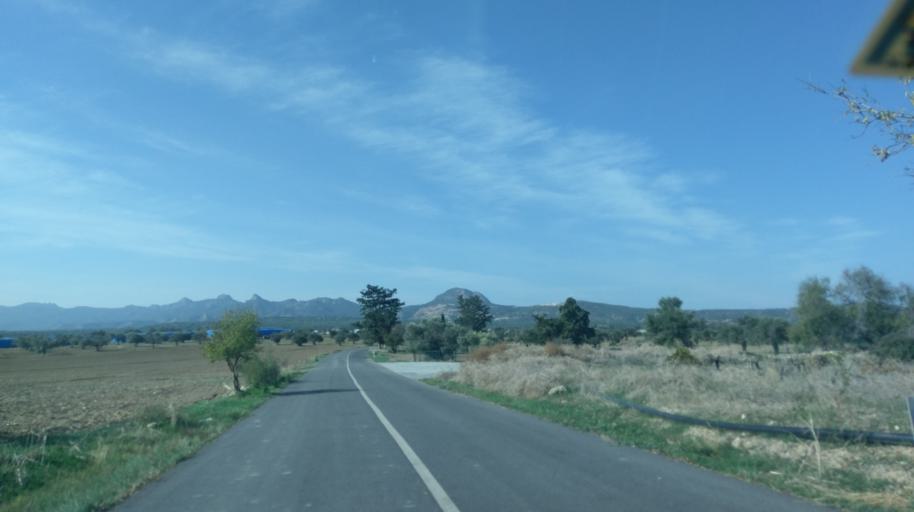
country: CY
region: Ammochostos
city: Leonarisso
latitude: 35.4062
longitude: 34.0120
